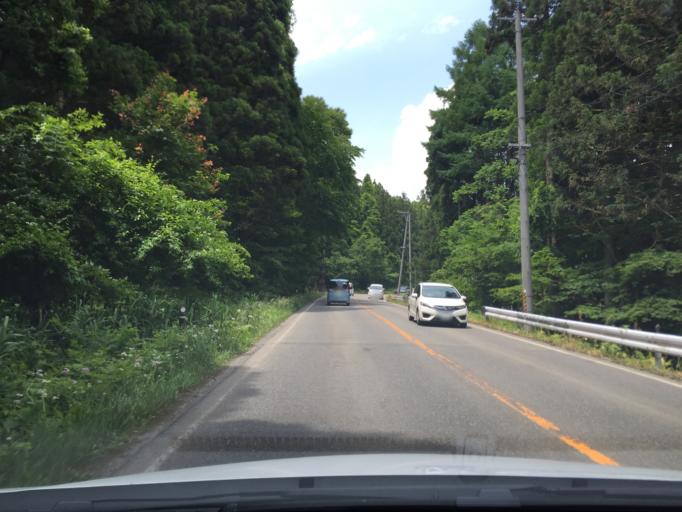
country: JP
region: Fukushima
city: Inawashiro
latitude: 37.6138
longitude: 140.1177
